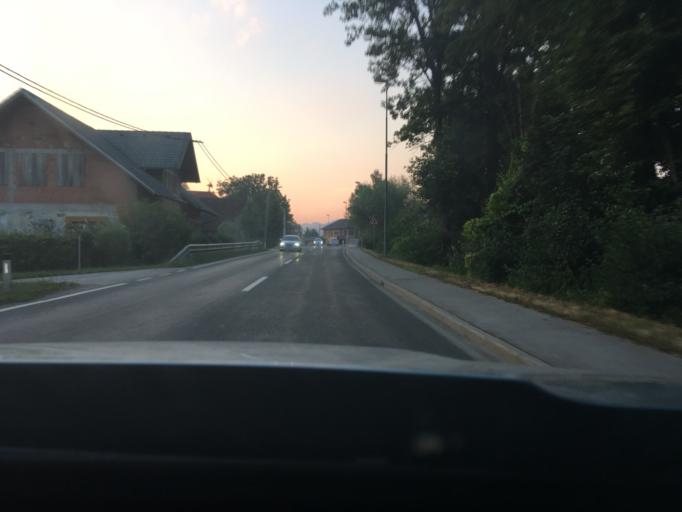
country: SI
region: Ribnica
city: Ribnica
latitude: 45.7299
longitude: 14.7371
